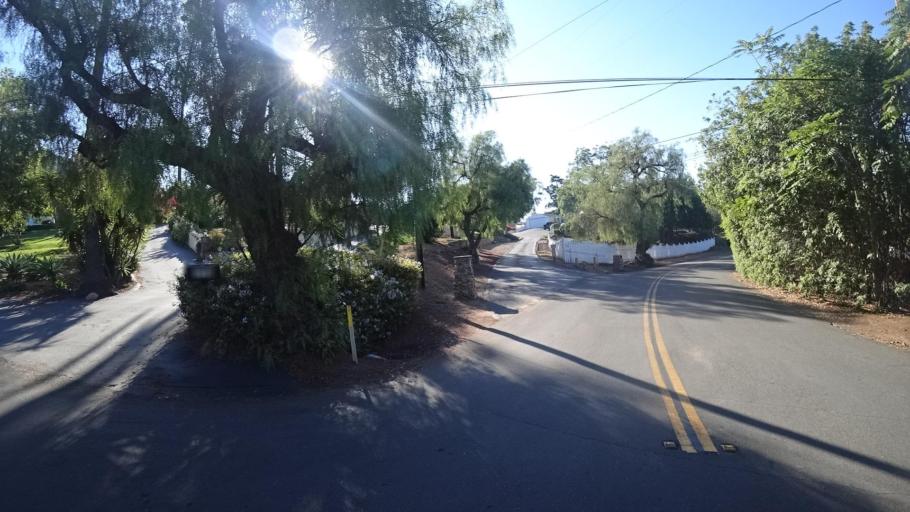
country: US
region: California
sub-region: San Diego County
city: La Mesa
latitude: 32.7736
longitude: -116.9956
